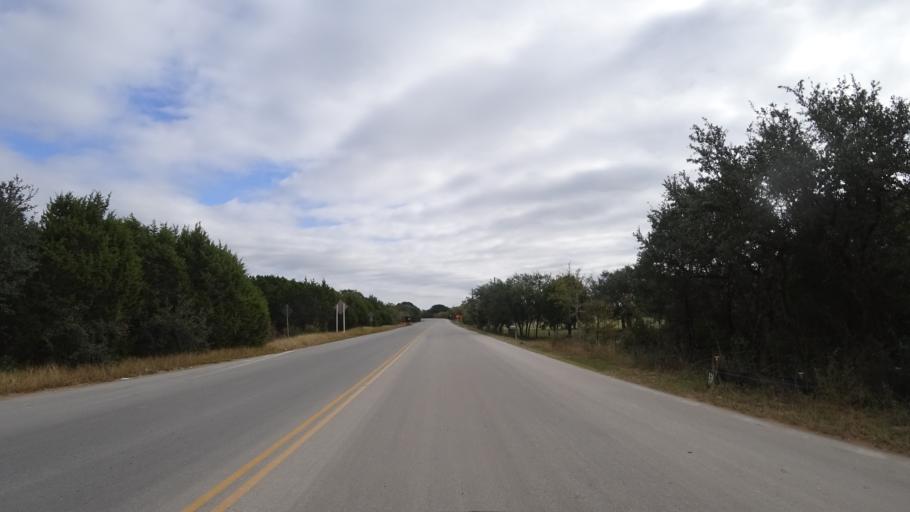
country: US
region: Texas
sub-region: Travis County
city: Shady Hollow
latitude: 30.1370
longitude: -97.8624
